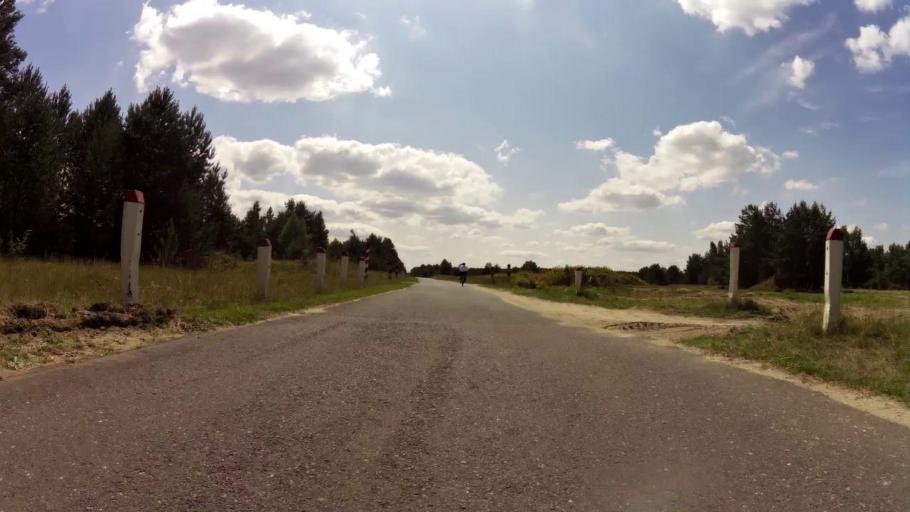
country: PL
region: West Pomeranian Voivodeship
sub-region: Powiat drawski
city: Drawsko Pomorskie
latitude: 53.3941
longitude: 15.7287
